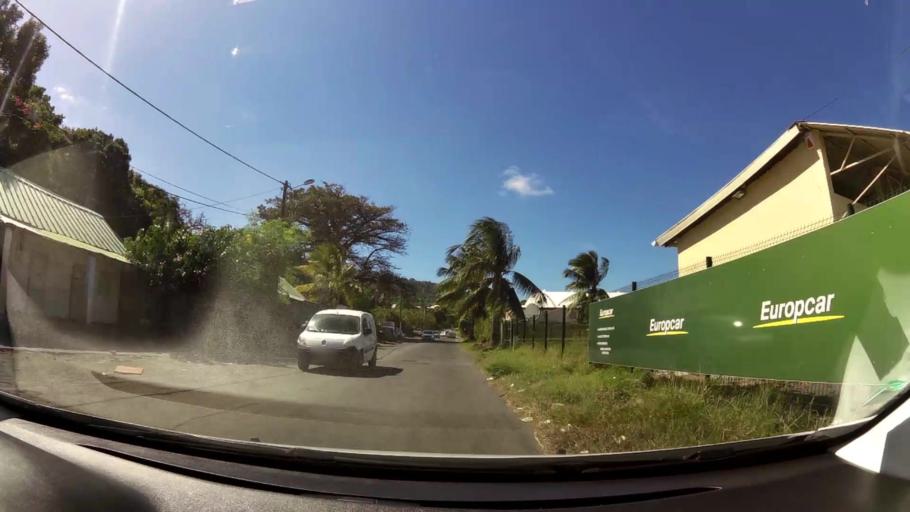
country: YT
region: Pamandzi
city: Pamandzi
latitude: -12.8024
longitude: 45.2807
